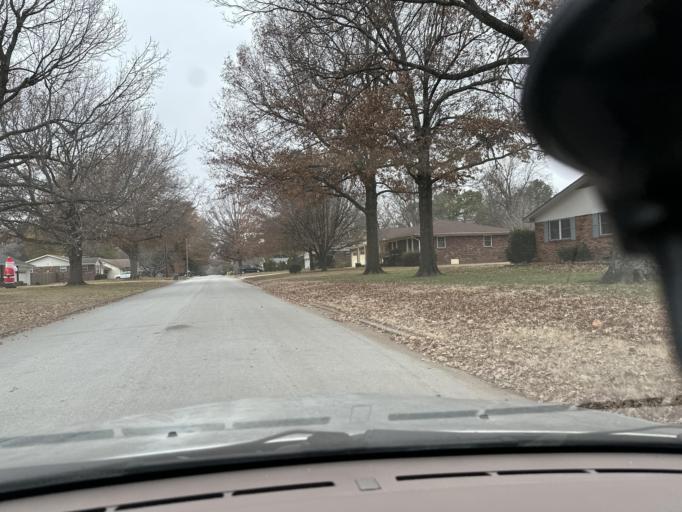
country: US
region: Arkansas
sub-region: Washington County
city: Johnson
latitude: 36.1096
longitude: -94.1370
